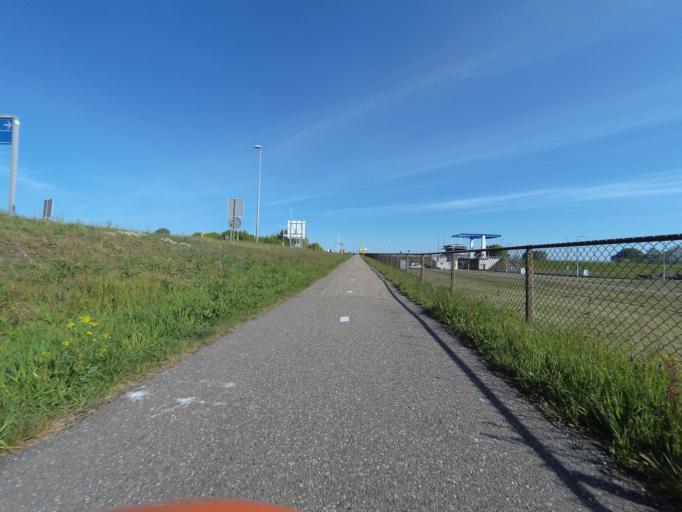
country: NL
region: Overijssel
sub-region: Gemeente Kampen
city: Kampen
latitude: 52.5436
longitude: 5.8546
